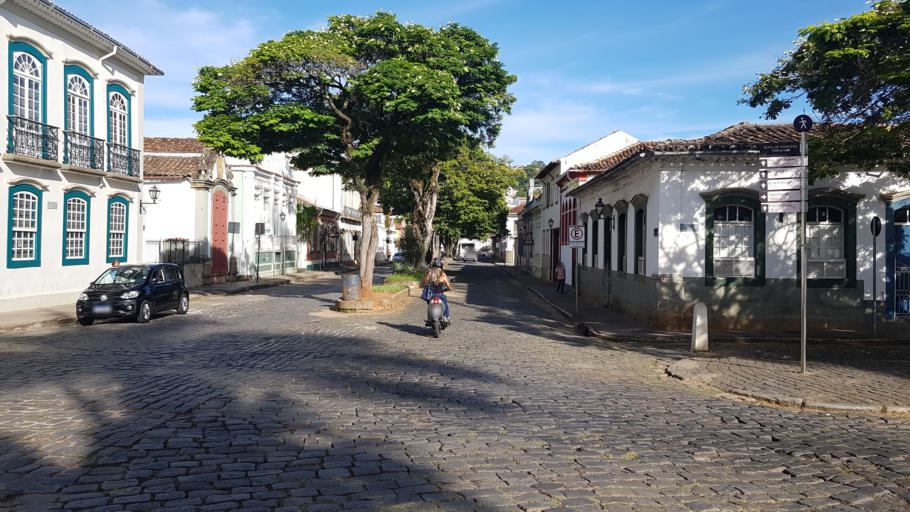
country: BR
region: Minas Gerais
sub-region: Sao Joao Del Rei
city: Sao Joao del Rei
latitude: -21.1385
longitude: -44.2610
